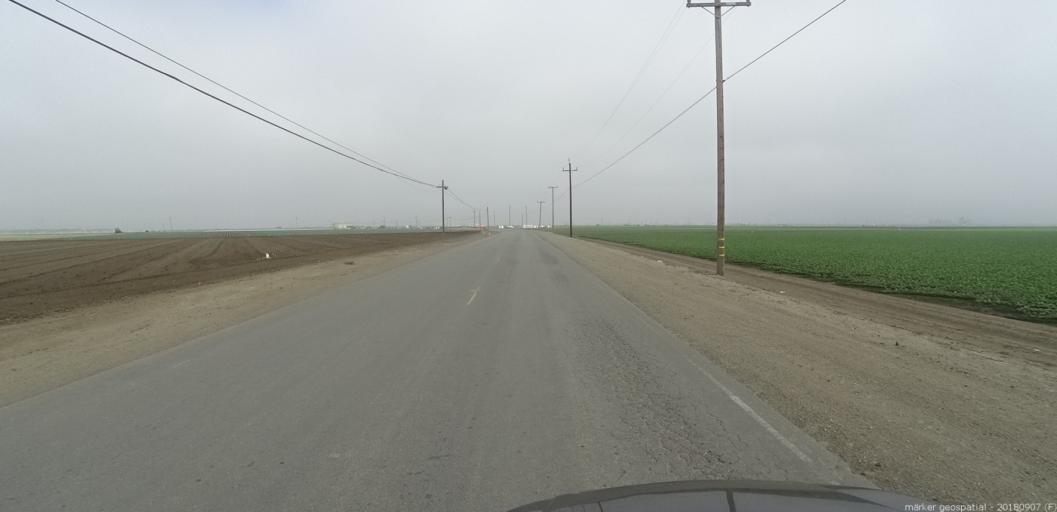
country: US
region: California
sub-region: Monterey County
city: Castroville
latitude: 36.7187
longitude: -121.7420
